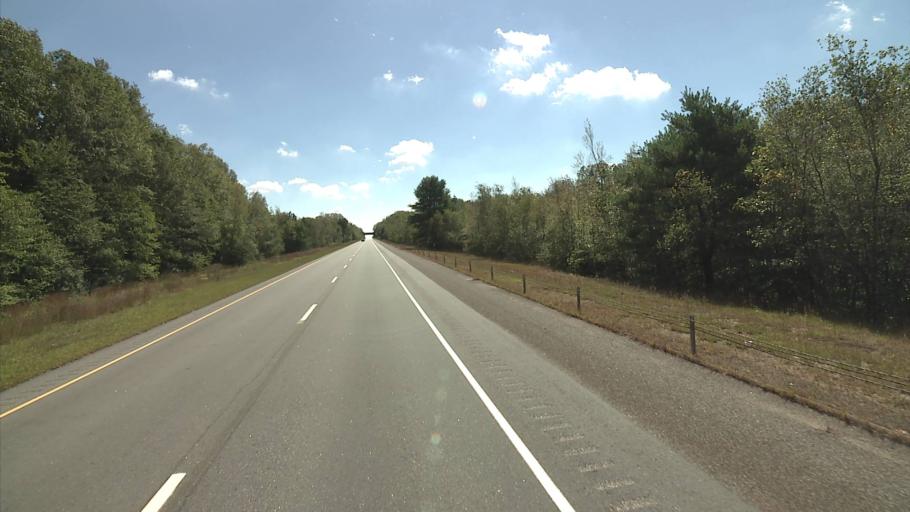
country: US
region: Connecticut
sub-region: New London County
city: Colchester
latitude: 41.5443
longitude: -72.3156
